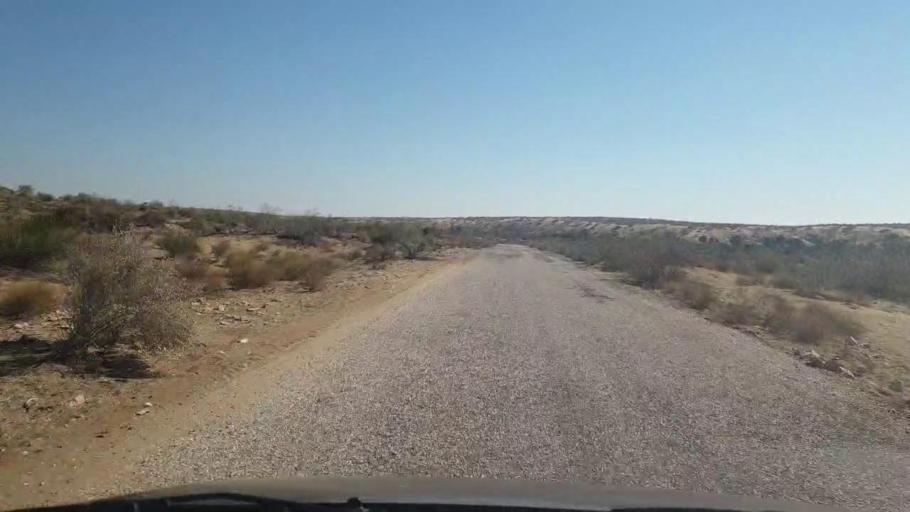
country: PK
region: Sindh
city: Bozdar
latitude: 27.0232
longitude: 68.7153
